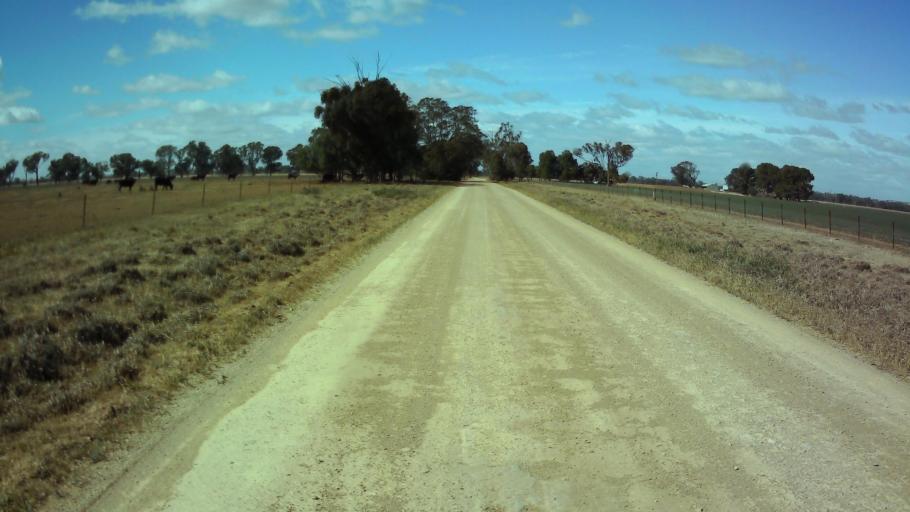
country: AU
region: New South Wales
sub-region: Weddin
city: Grenfell
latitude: -34.0257
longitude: 148.3182
